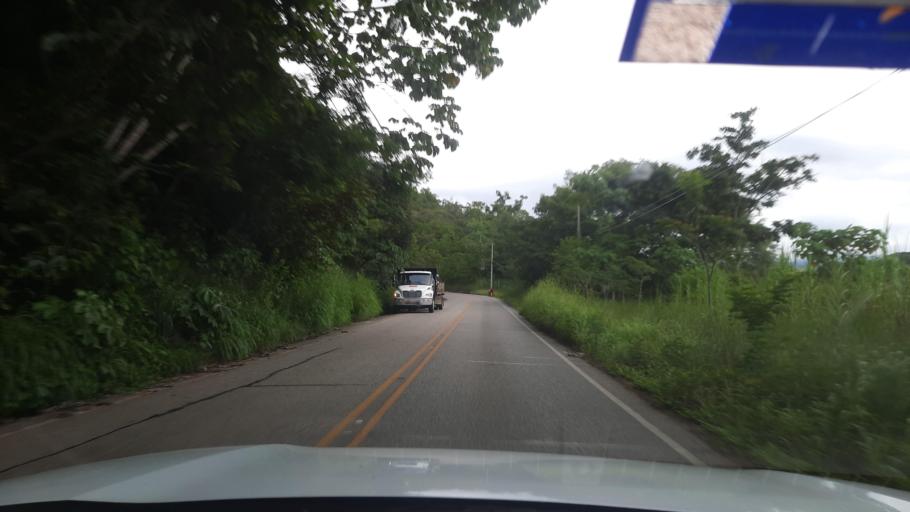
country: CR
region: Puntarenas
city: Buenos Aires
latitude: 9.0032
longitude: -83.2264
